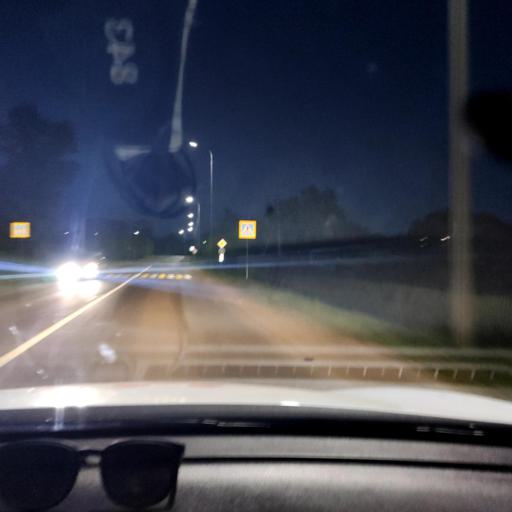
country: RU
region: Tatarstan
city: Rybnaya Sloboda
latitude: 55.4715
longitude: 50.0200
